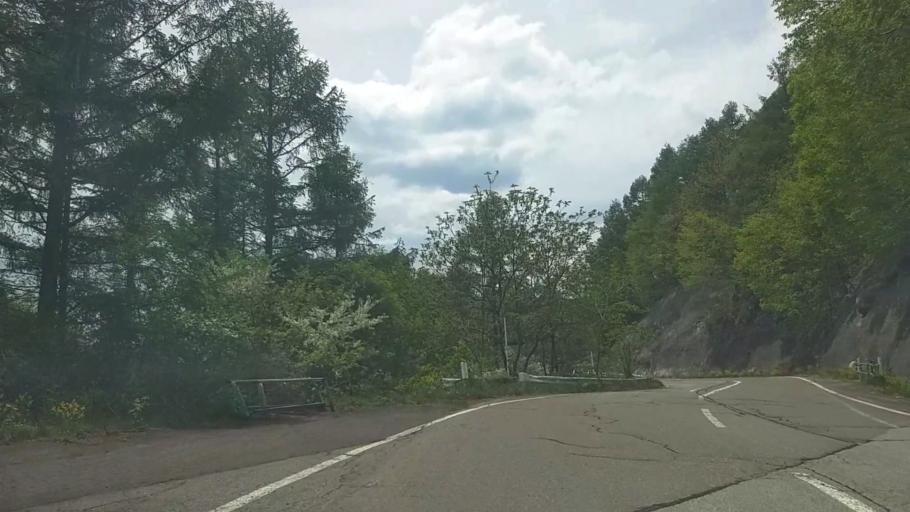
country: JP
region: Nagano
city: Saku
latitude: 36.1045
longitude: 138.3976
